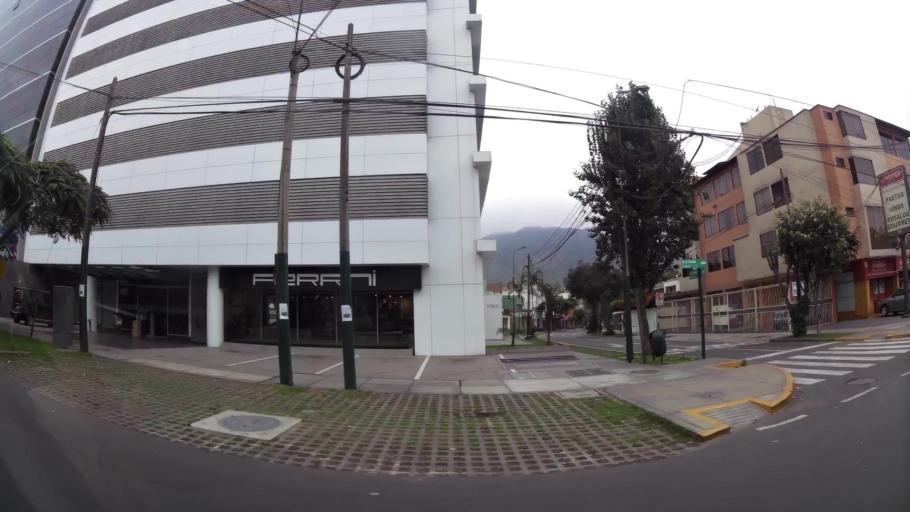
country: PE
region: Lima
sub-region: Lima
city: La Molina
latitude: -12.1061
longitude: -76.9712
